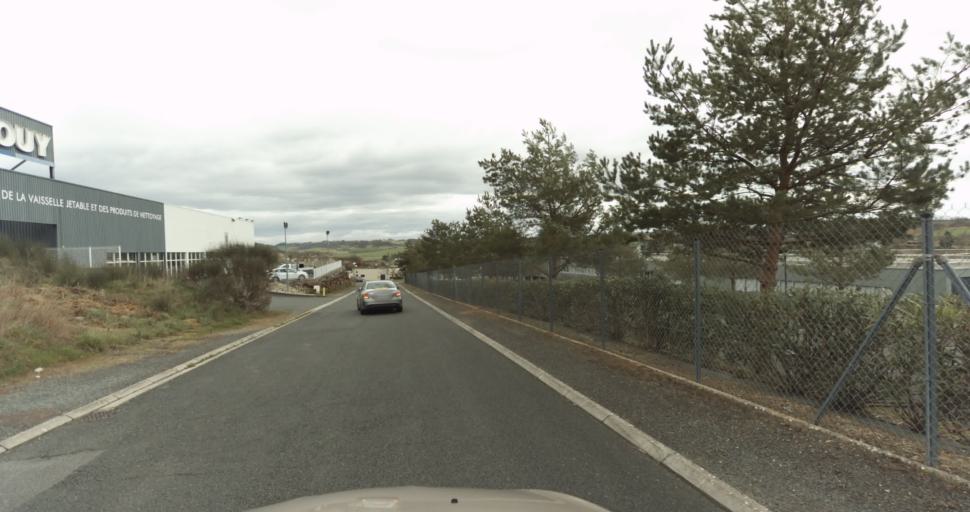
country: FR
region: Midi-Pyrenees
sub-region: Departement du Tarn
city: Puygouzon
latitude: 43.8943
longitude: 2.1653
